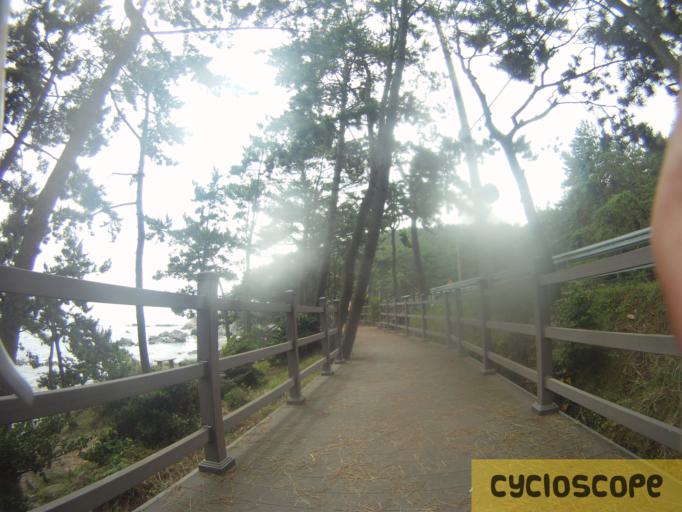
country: KR
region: Busan
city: Kijang
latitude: 35.2781
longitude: 129.2549
